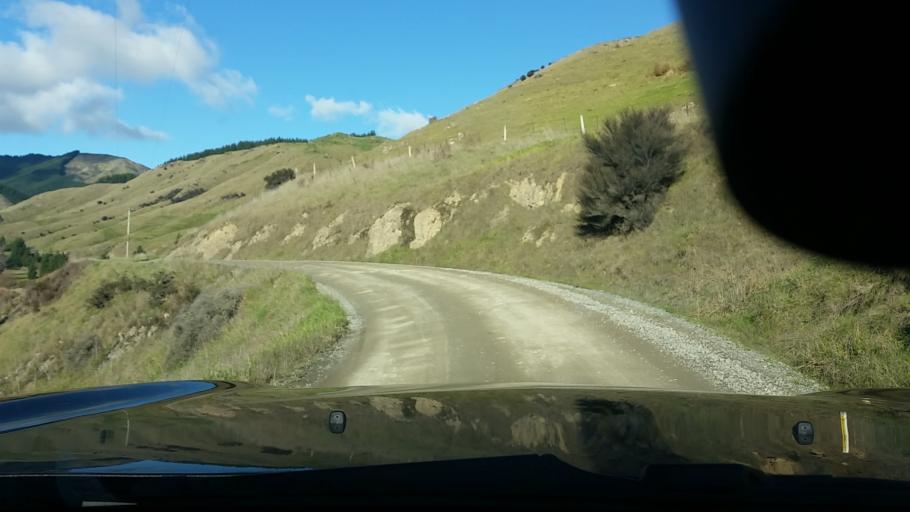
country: NZ
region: Marlborough
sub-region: Marlborough District
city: Blenheim
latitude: -41.6007
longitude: 173.9533
